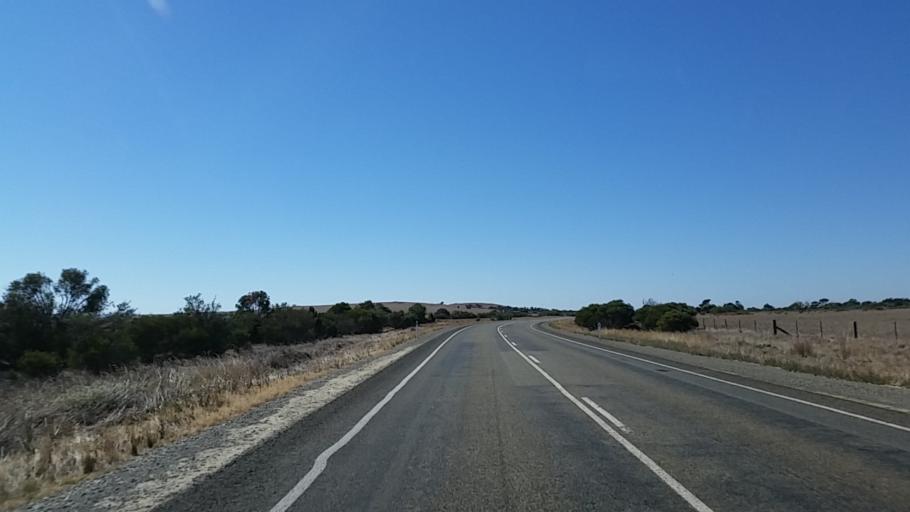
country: AU
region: South Australia
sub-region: Peterborough
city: Peterborough
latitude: -33.2349
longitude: 138.8779
